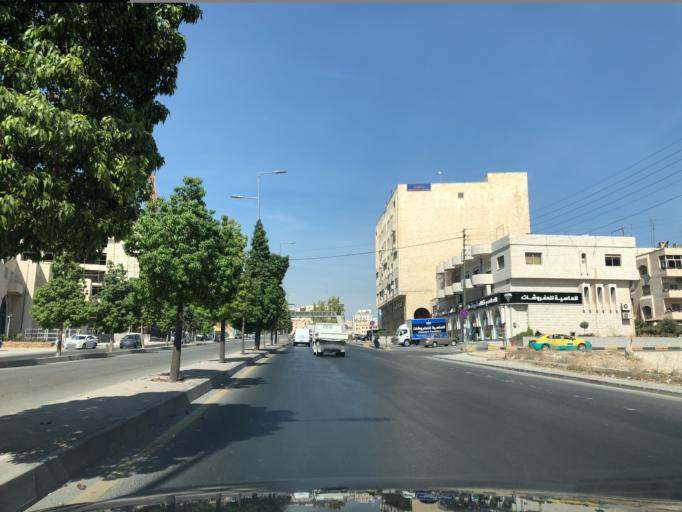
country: JO
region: Amman
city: Al Jubayhah
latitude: 32.0217
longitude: 35.8615
